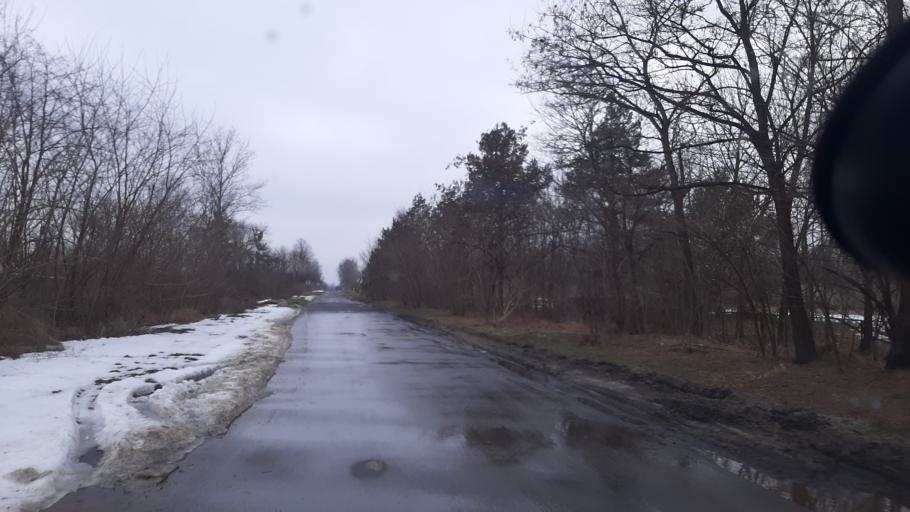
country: PL
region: Lublin Voivodeship
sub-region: Powiat wlodawski
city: Wlodawa
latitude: 51.5182
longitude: 23.5921
